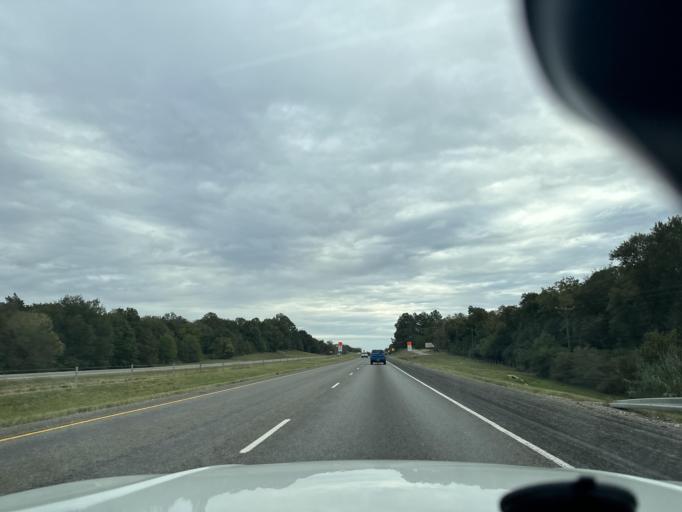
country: US
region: Texas
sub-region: Washington County
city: Brenham
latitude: 30.1825
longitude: -96.4824
